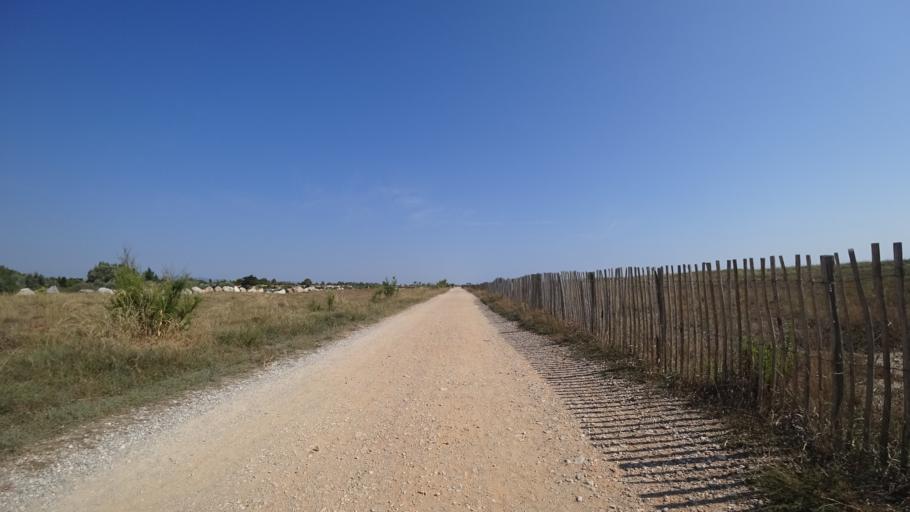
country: FR
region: Languedoc-Roussillon
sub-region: Departement des Pyrenees-Orientales
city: Le Barcares
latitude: 42.7589
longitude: 3.0371
